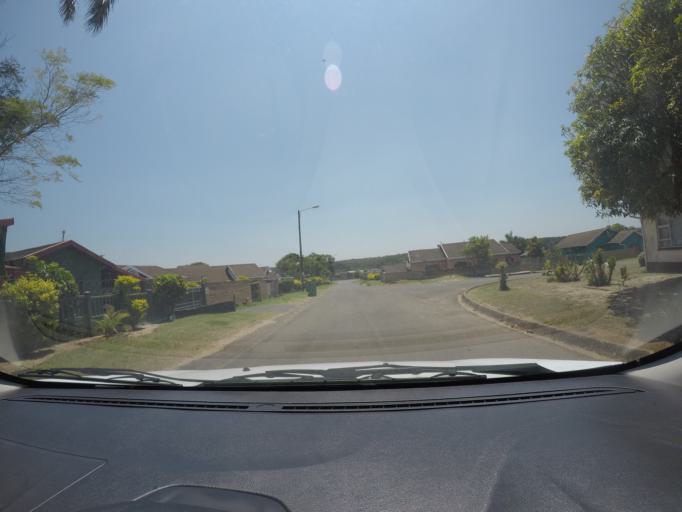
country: ZA
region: KwaZulu-Natal
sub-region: uThungulu District Municipality
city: eSikhawini
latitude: -28.8902
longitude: 31.8833
